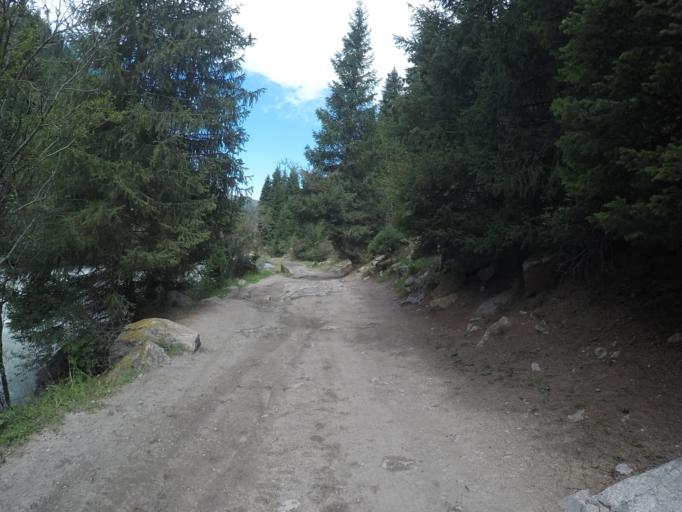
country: KG
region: Ysyk-Koel
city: Teploklyuchenka
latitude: 42.4431
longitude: 78.5516
